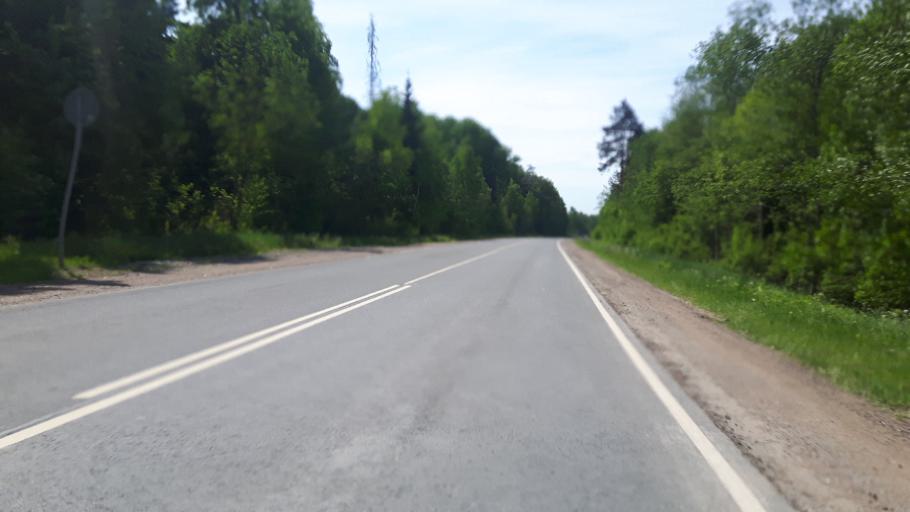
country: RU
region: Leningrad
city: Vistino
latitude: 59.6870
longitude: 28.4605
